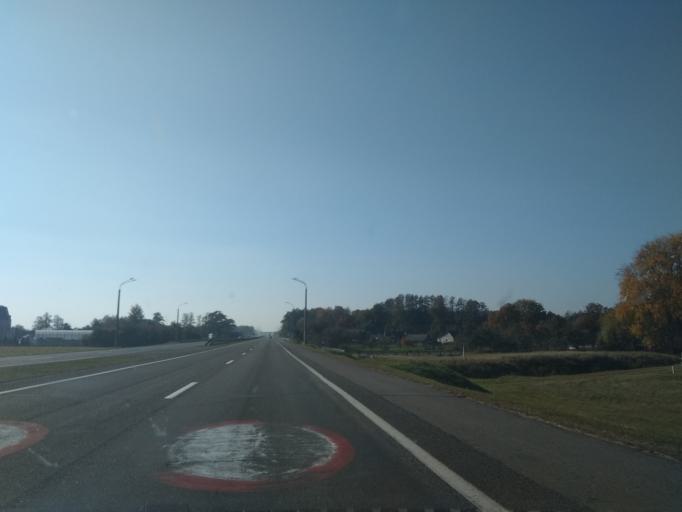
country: BY
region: Brest
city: Horad Kobryn
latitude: 52.1857
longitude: 24.3916
